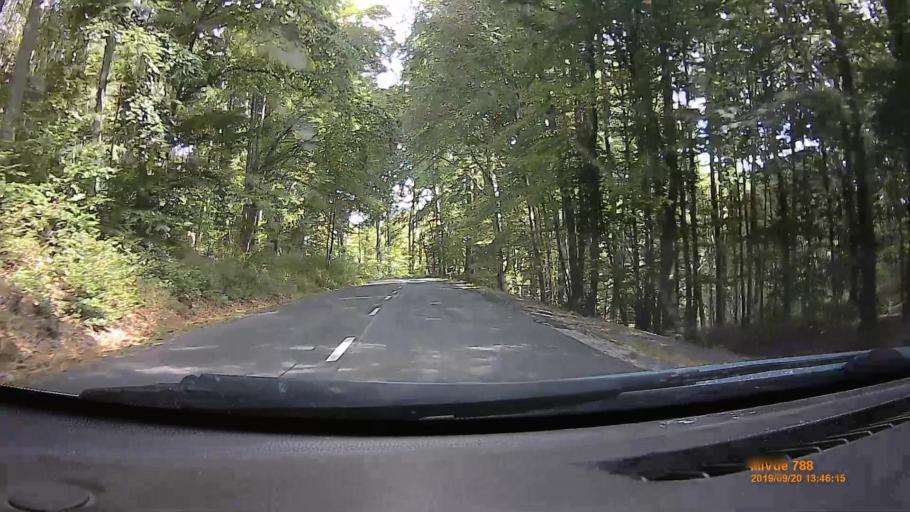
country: HU
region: Borsod-Abauj-Zemplen
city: Saly
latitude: 48.0632
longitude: 20.5694
